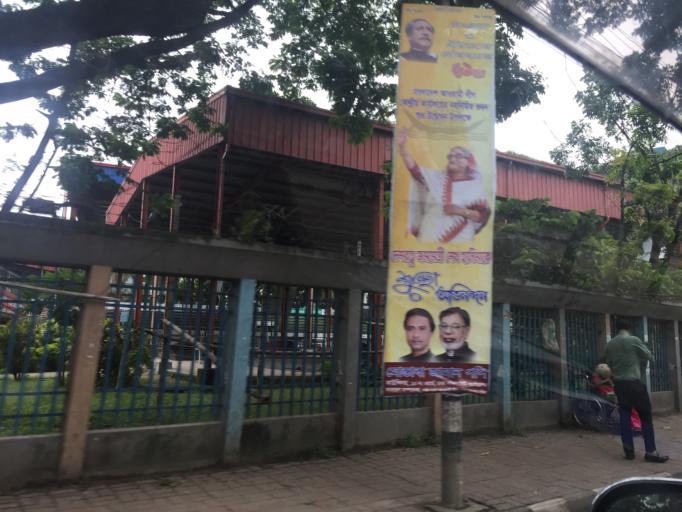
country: BD
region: Dhaka
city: Paltan
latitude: 23.7249
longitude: 90.4136
